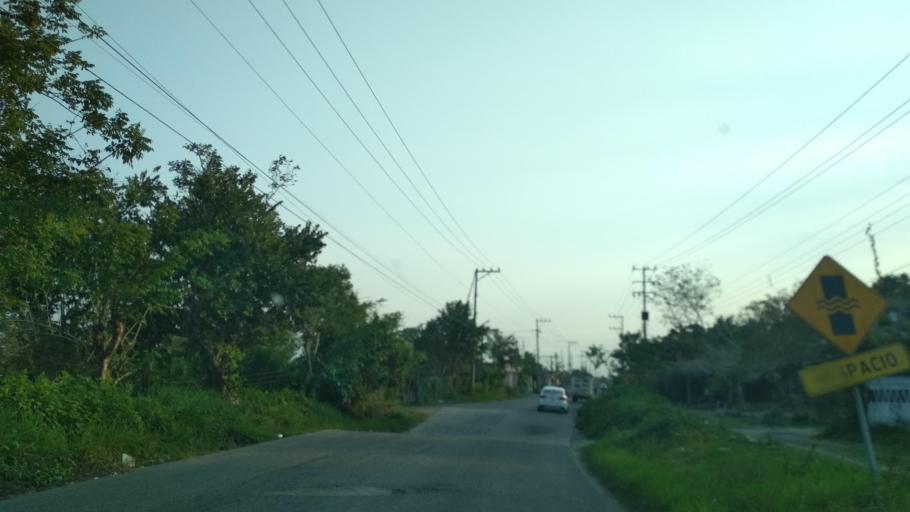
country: MM
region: Shan
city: Taunggyi
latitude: 20.4123
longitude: 97.3366
